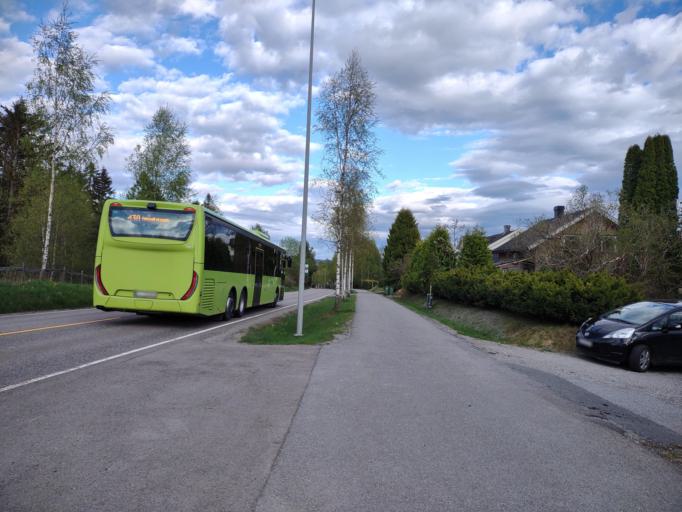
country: NO
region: Akershus
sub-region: Eidsvoll
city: Eidsvoll
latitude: 60.3232
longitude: 11.2323
